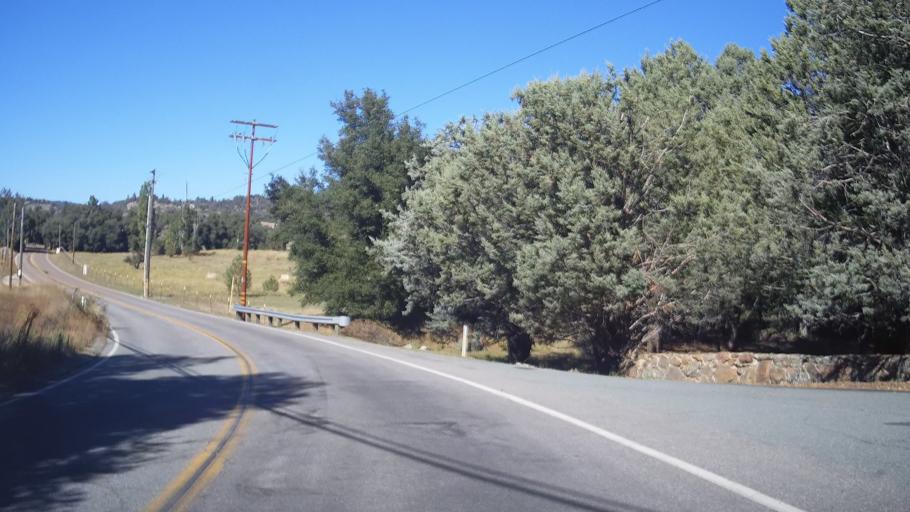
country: US
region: California
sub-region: San Diego County
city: Julian
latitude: 33.0676
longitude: -116.6181
